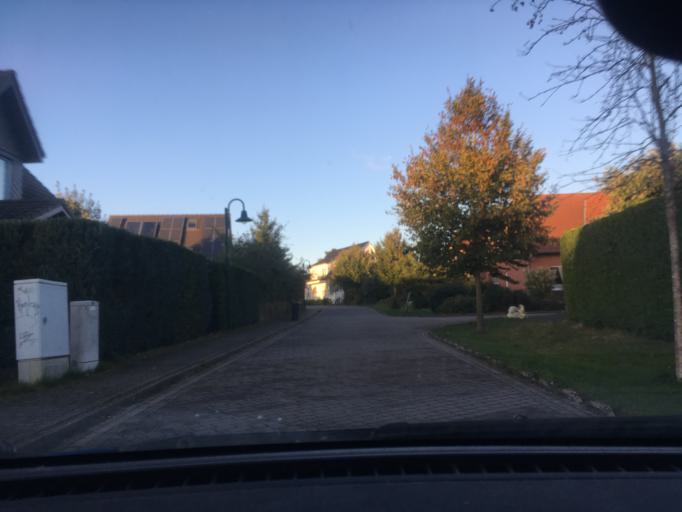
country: DE
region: Lower Saxony
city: Deutsch Evern
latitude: 53.2017
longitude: 10.4355
